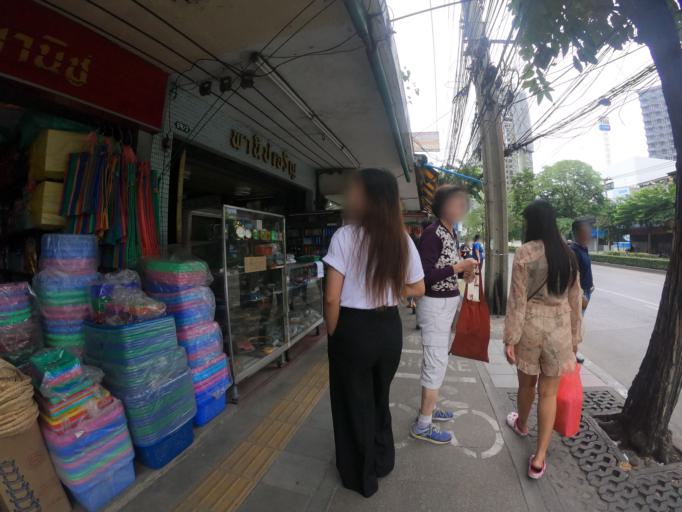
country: TH
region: Bangkok
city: Chatuchak
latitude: 13.8120
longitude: 100.5631
